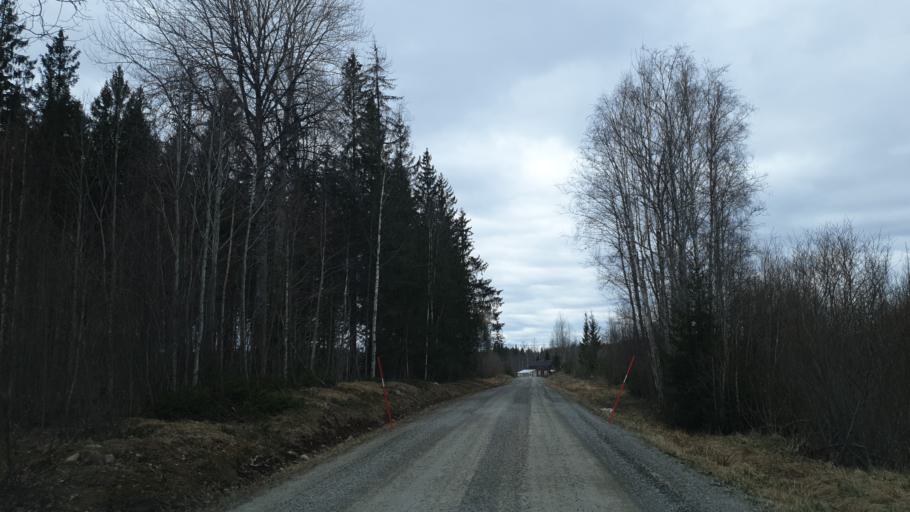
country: SE
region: OErebro
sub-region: Nora Kommun
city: As
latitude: 59.5996
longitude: 14.9168
